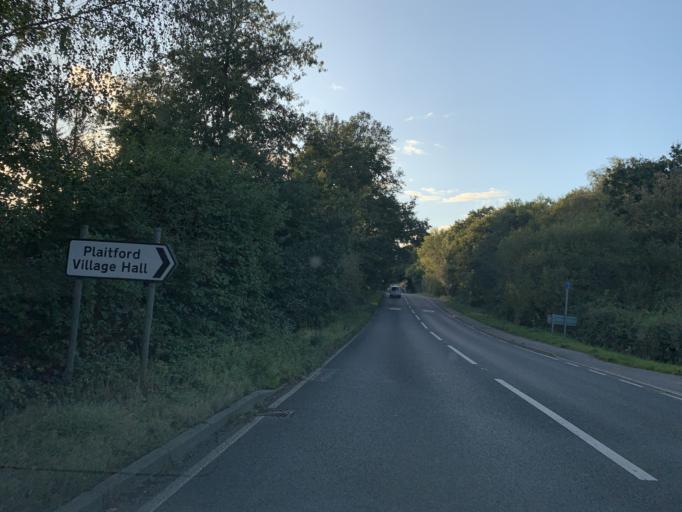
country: GB
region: England
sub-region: Hampshire
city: West Wellow
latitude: 50.9724
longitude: -1.6025
